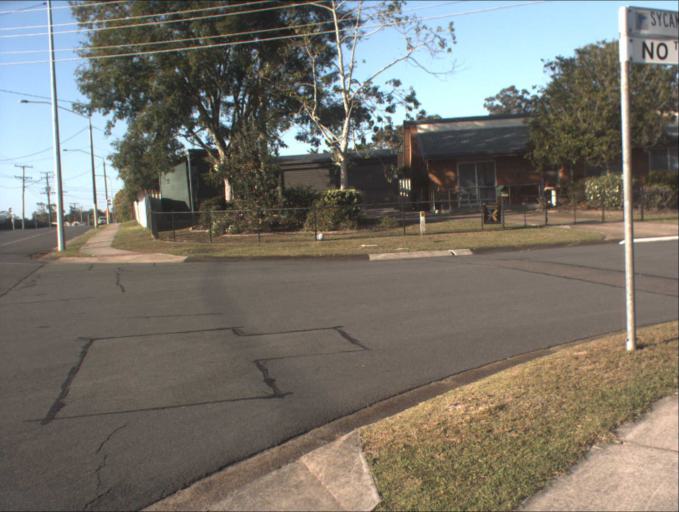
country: AU
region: Queensland
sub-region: Logan
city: Logan City
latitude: -27.6492
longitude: 153.0992
